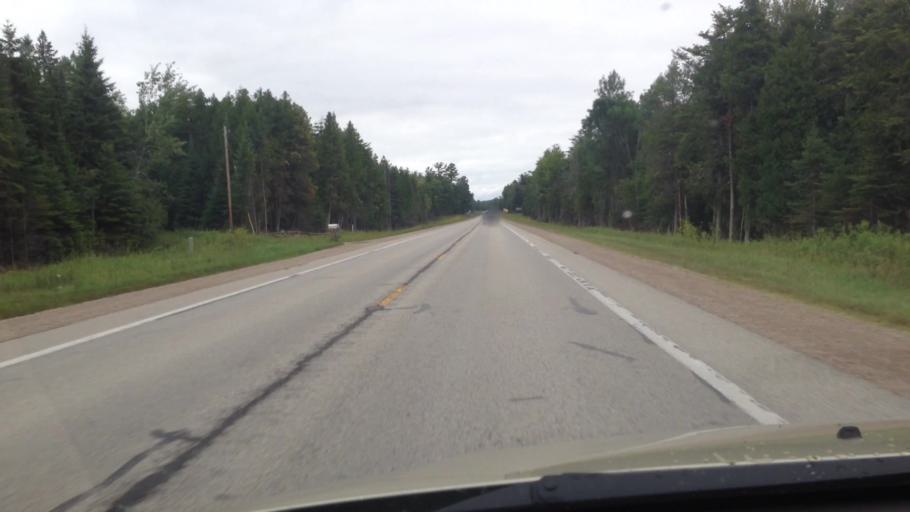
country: US
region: Michigan
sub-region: Delta County
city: Escanaba
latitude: 45.5734
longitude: -87.2504
